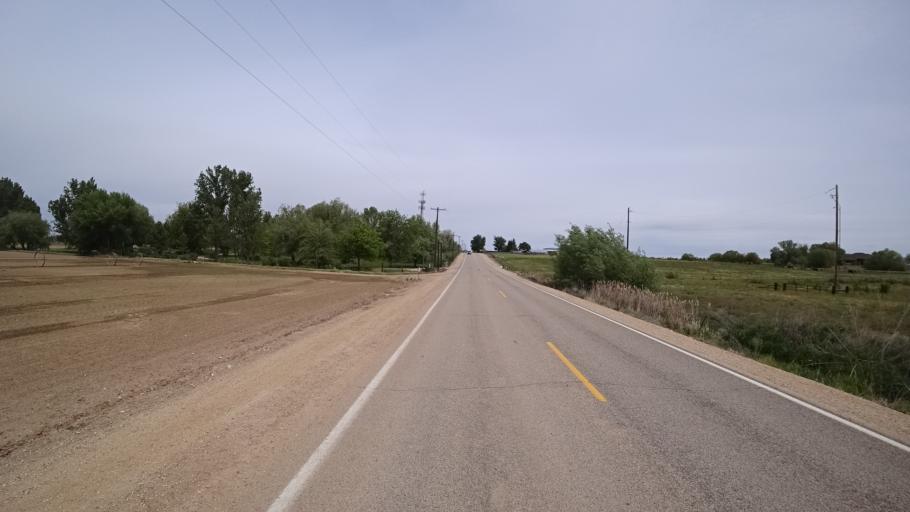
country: US
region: Idaho
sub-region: Ada County
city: Kuna
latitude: 43.5571
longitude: -116.4737
